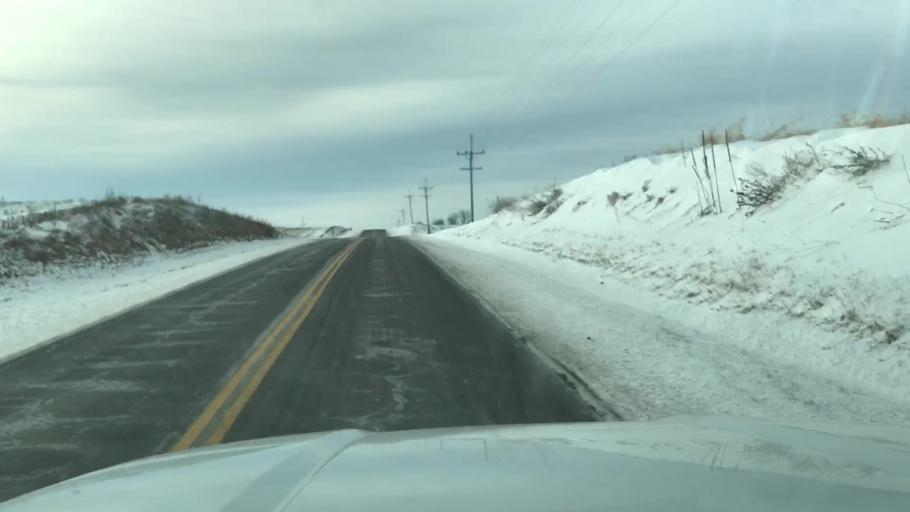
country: US
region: Missouri
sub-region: Holt County
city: Mound City
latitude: 40.1061
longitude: -95.1449
